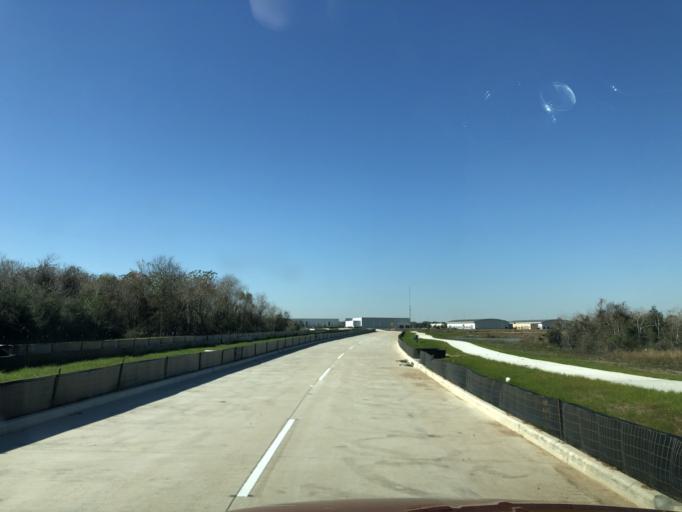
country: US
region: Texas
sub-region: Brazoria County
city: Brookside Village
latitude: 29.5886
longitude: -95.3933
